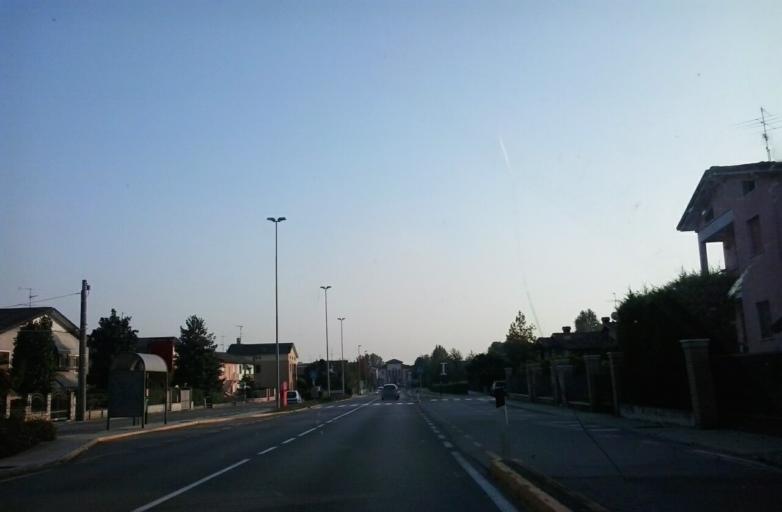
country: IT
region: Lombardy
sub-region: Provincia di Brescia
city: Poncarale
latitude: 45.4645
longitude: 10.1741
